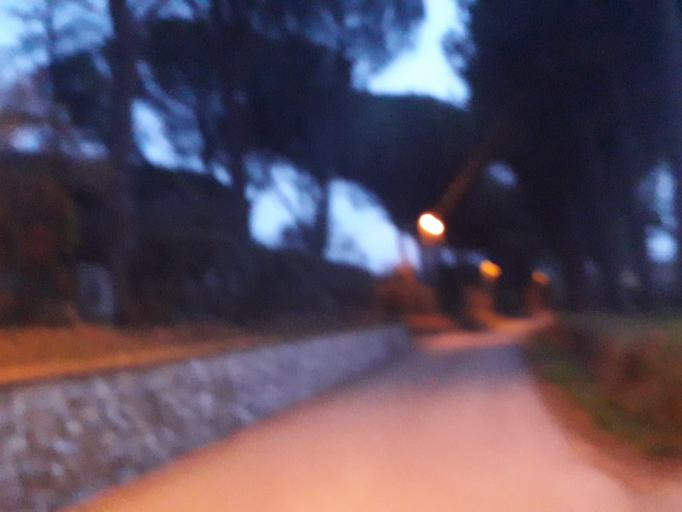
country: IT
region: Umbria
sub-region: Provincia di Perugia
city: Perugia
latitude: 43.0867
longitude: 12.4030
